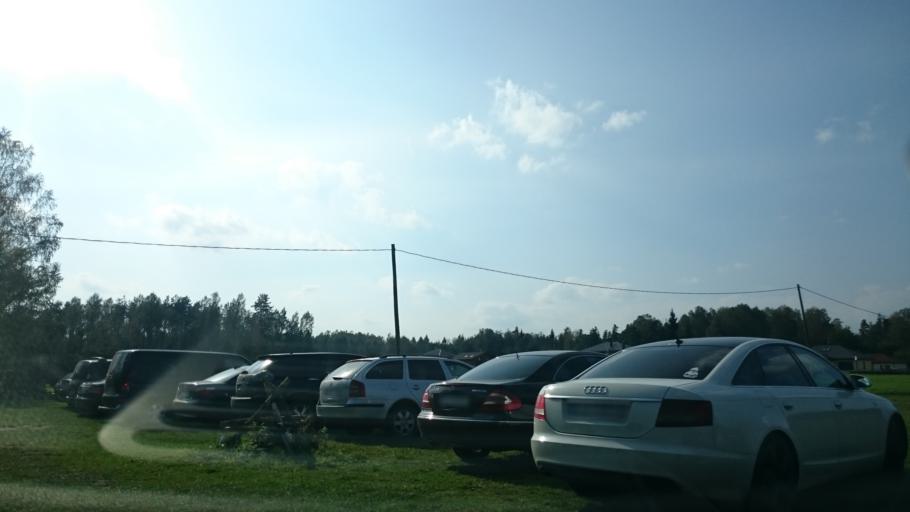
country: LV
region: Stopini
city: Ulbroka
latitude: 56.9205
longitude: 24.3361
